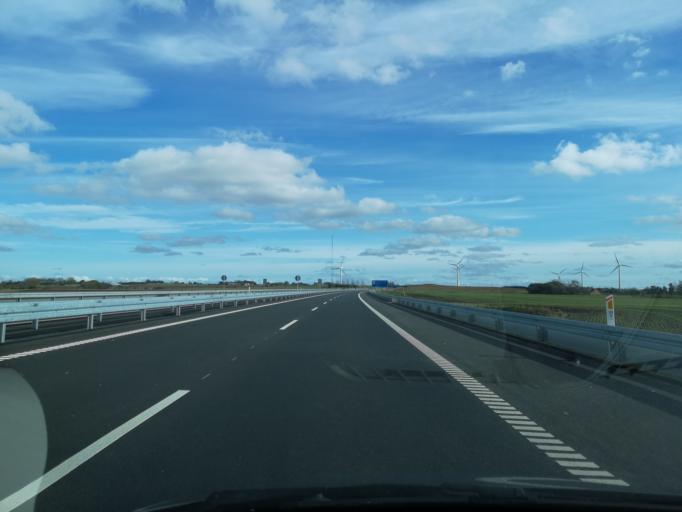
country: DK
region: Central Jutland
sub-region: Holstebro Kommune
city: Holstebro
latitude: 56.3883
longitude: 8.6385
